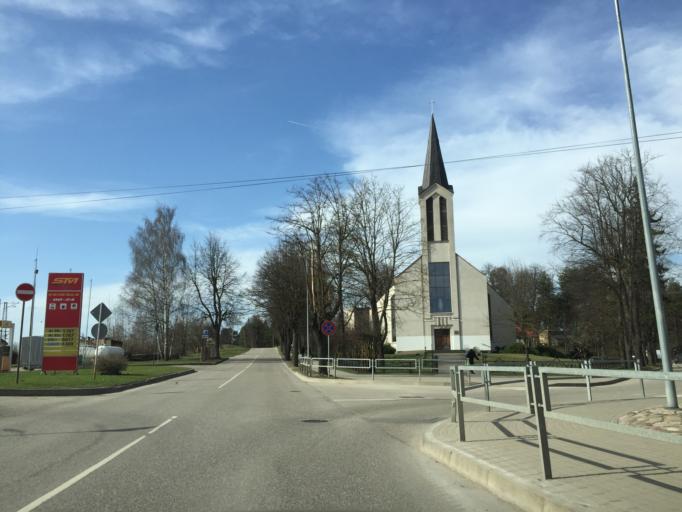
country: LV
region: Ogre
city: Ogre
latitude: 56.8174
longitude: 24.6003
